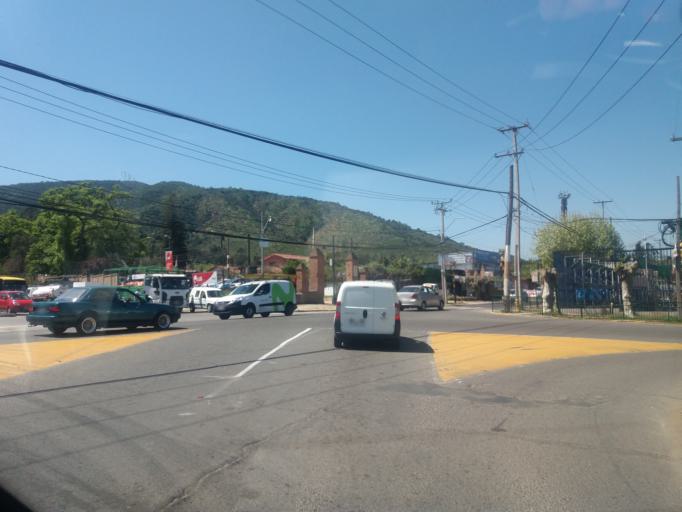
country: CL
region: Valparaiso
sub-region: Provincia de Marga Marga
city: Limache
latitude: -32.9823
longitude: -71.2759
